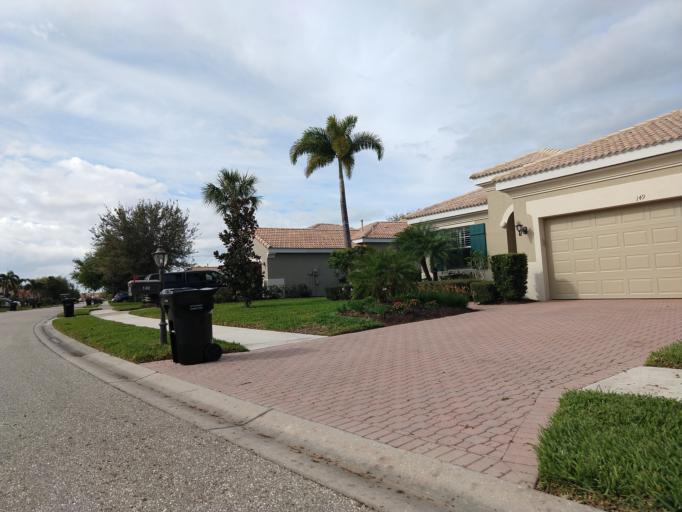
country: US
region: Florida
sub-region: Sarasota County
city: Nokomis
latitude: 27.1491
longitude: -82.3738
